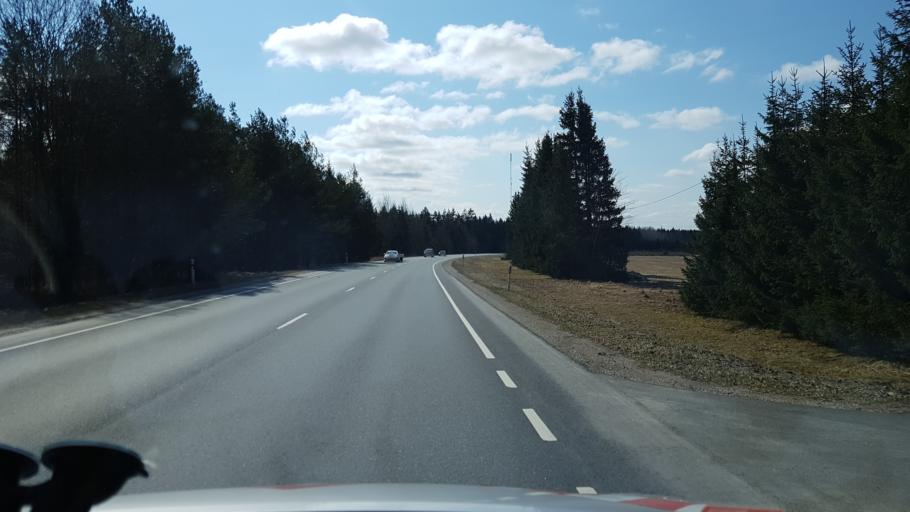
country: EE
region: Harju
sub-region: Nissi vald
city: Turba
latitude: 59.0391
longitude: 24.1676
